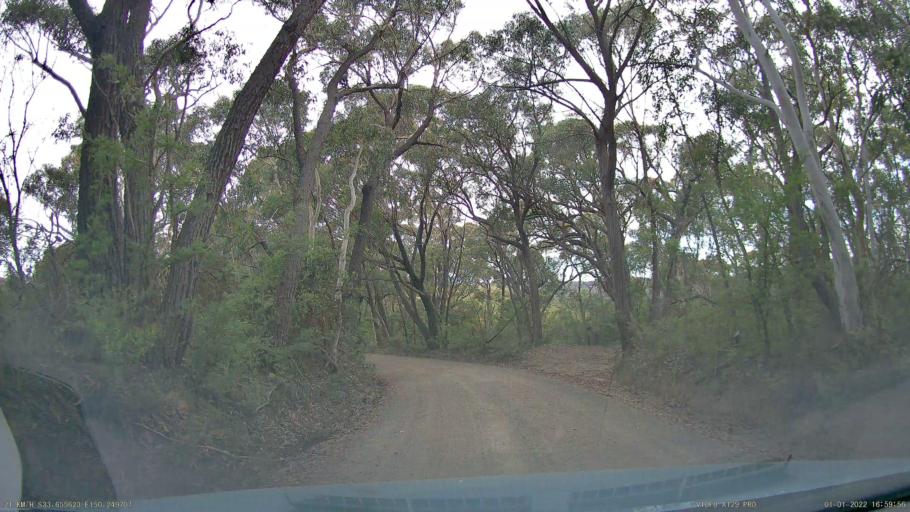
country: AU
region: New South Wales
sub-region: Blue Mountains Municipality
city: Blackheath
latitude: -33.6557
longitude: 150.2497
